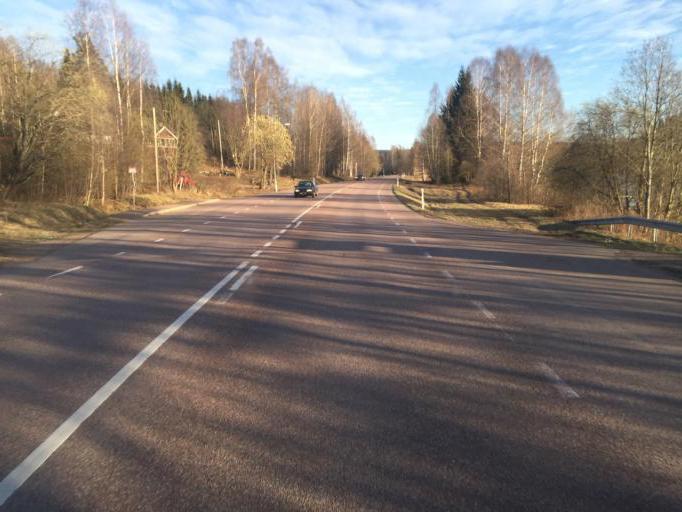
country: SE
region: Dalarna
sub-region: Gagnefs Kommun
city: Djuras
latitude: 60.5450
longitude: 15.2783
